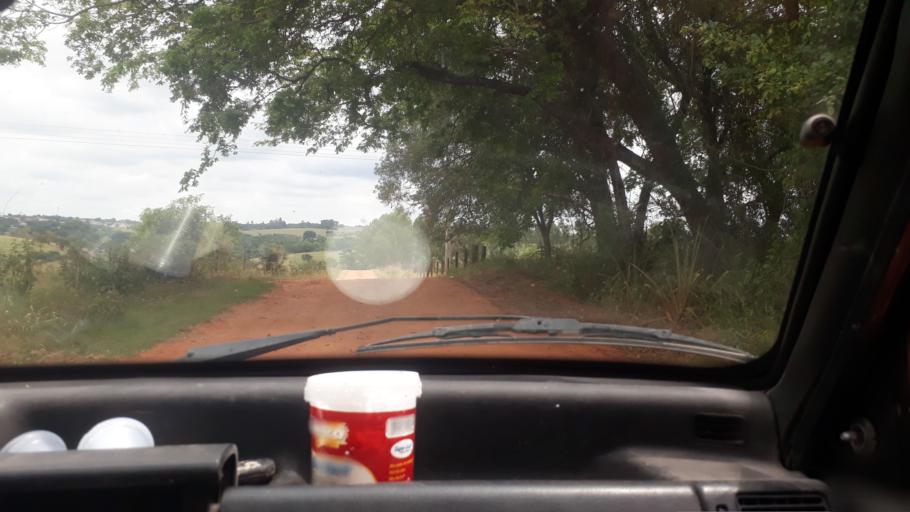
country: BR
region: Sao Paulo
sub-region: Regente Feijo
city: Regente Feijo
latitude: -22.2480
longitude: -51.2976
